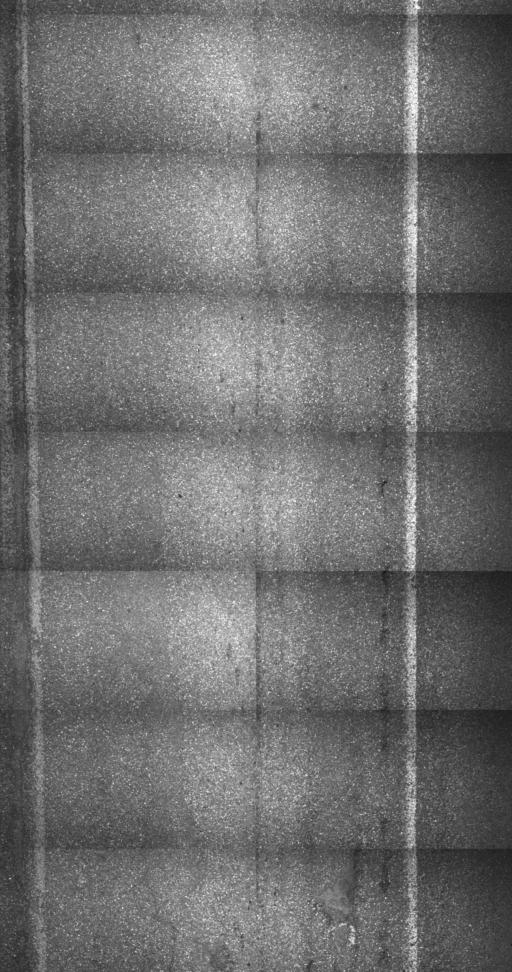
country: US
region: Vermont
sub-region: Caledonia County
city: Hardwick
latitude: 44.5176
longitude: -72.4053
